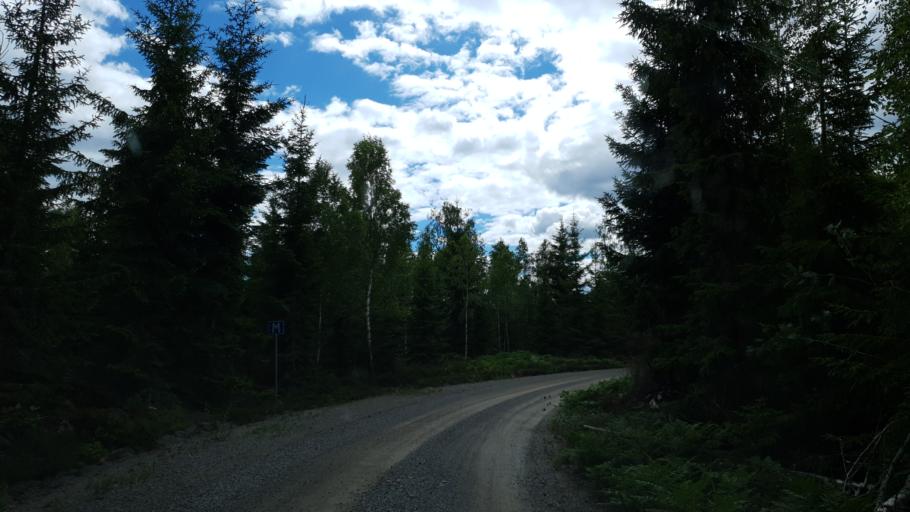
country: SE
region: Kalmar
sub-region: Hultsfreds Kommun
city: Virserum
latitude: 57.0874
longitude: 15.6206
